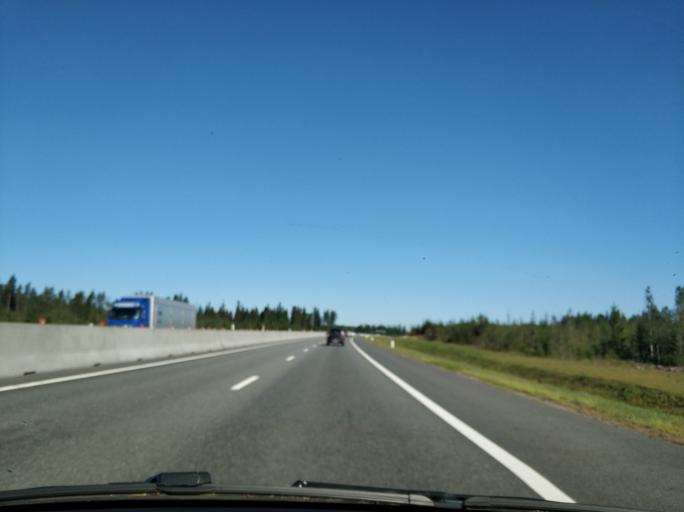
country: RU
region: Leningrad
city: Sosnovo
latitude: 60.4407
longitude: 30.2133
